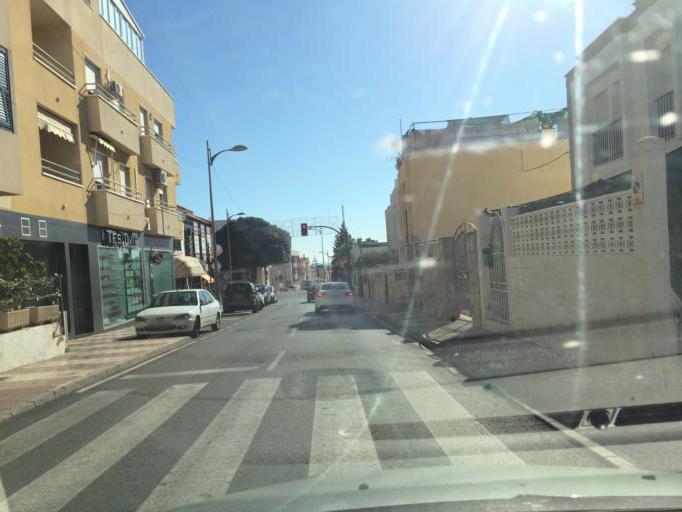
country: ES
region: Andalusia
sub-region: Provincia de Almeria
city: Aguadulce
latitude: 36.8091
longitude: -2.5881
